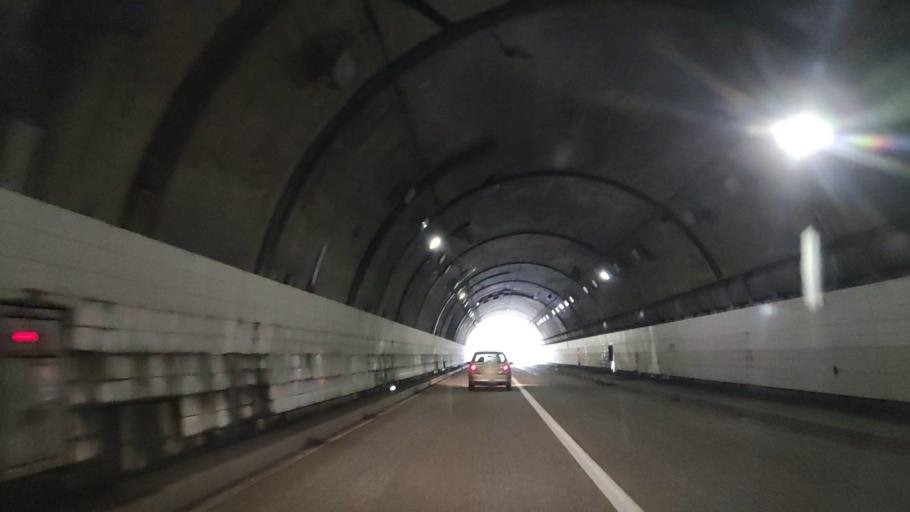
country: JP
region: Akita
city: Takanosu
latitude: 40.2172
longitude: 140.2340
